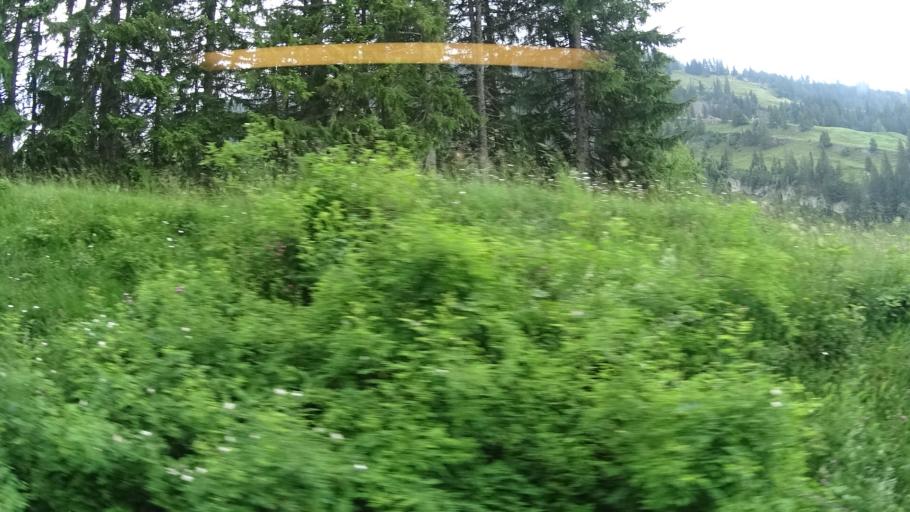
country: CH
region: Lucerne
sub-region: Lucerne-Land District
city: Vitznau
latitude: 47.0430
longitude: 8.4842
